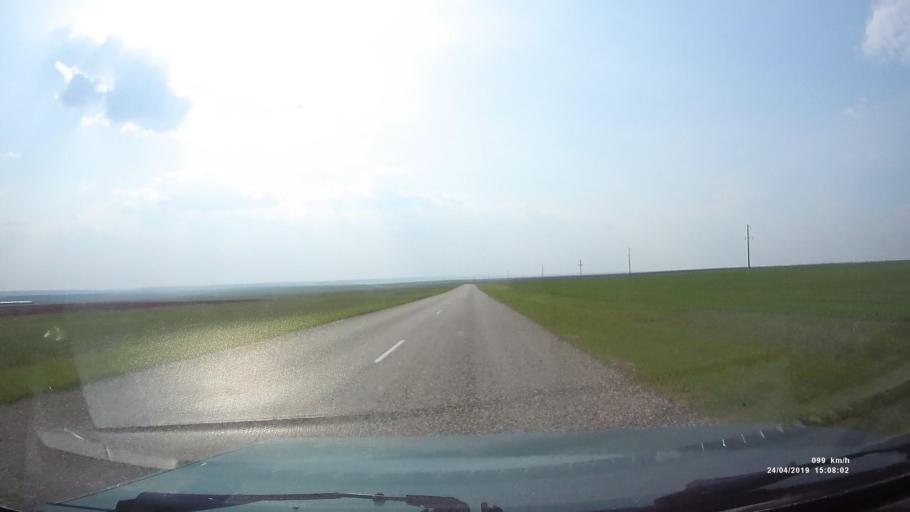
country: RU
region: Rostov
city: Remontnoye
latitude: 46.5599
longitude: 43.3917
